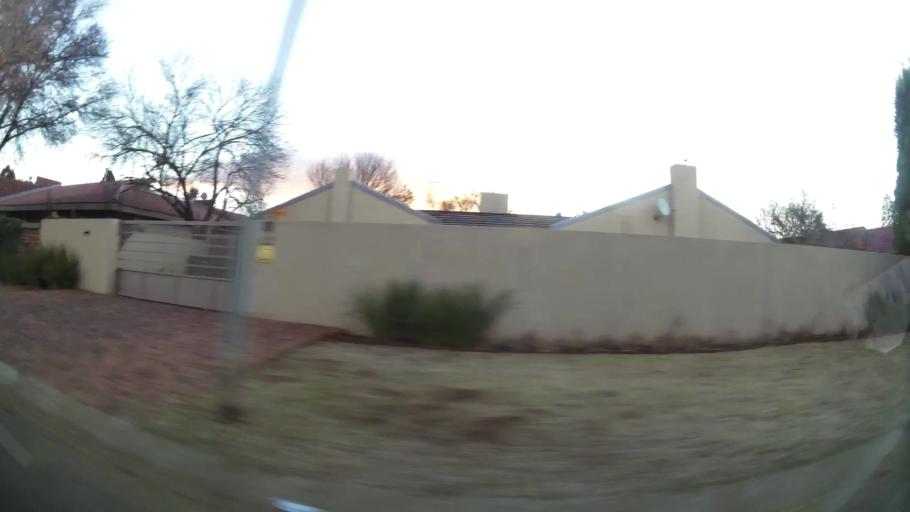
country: ZA
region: North-West
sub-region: Dr Kenneth Kaunda District Municipality
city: Potchefstroom
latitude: -26.7194
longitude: 27.1232
